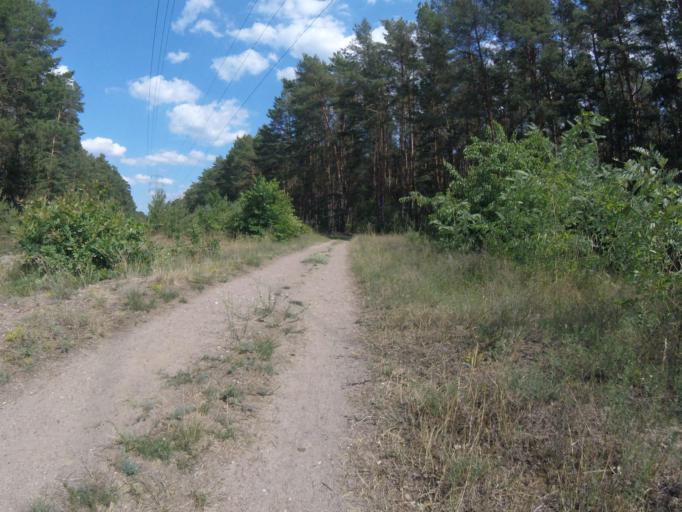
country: DE
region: Brandenburg
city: Wildau
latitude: 52.3335
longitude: 13.6643
